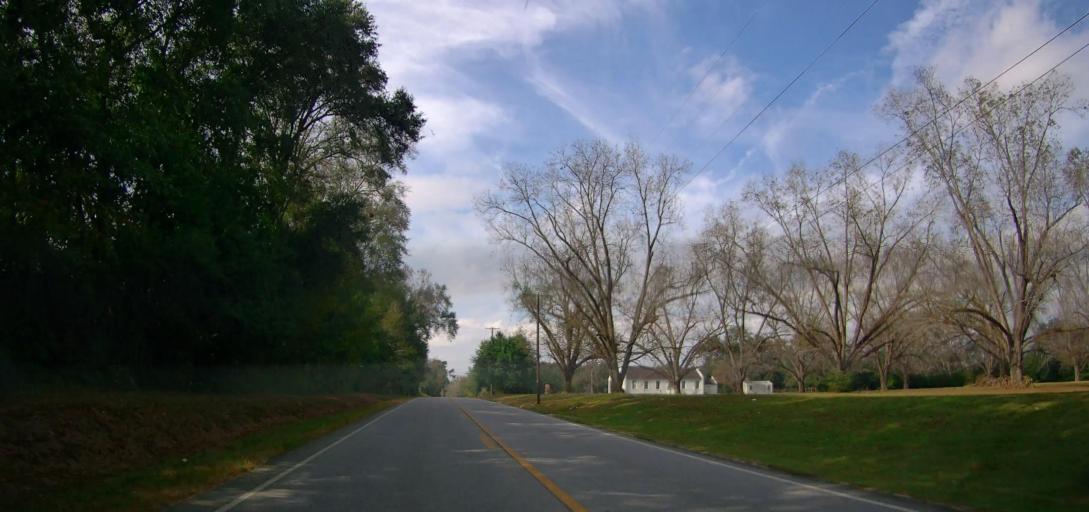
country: US
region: Georgia
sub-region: Thomas County
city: Thomasville
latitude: 30.9301
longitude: -84.0218
